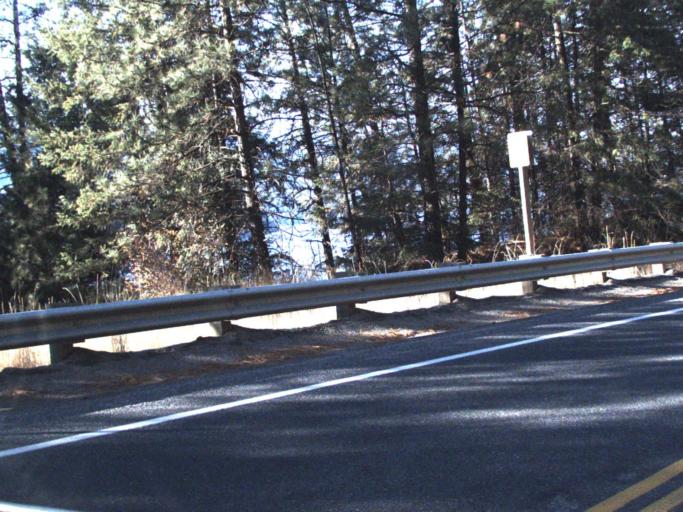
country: US
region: Washington
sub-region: Stevens County
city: Kettle Falls
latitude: 48.6148
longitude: -118.0784
